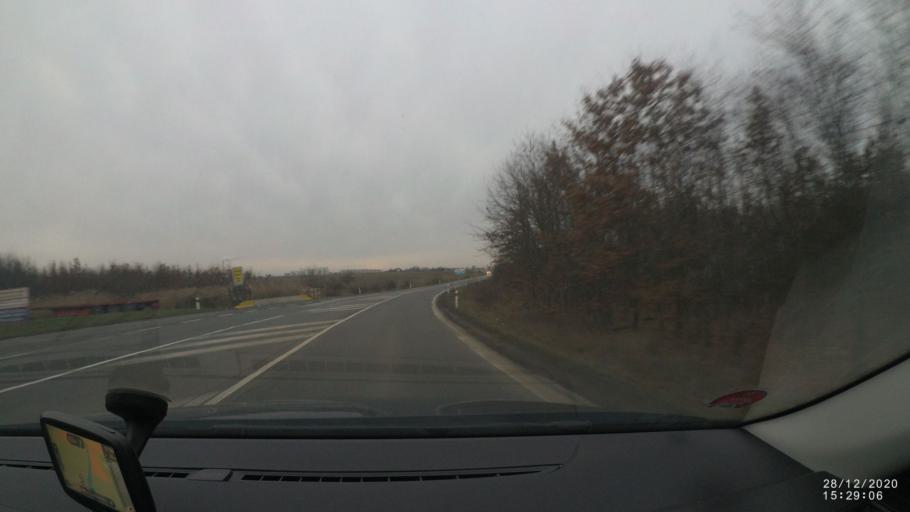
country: CZ
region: Praha
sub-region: Praha 14
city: Dolni Pocernice
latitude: 50.0824
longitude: 14.5859
